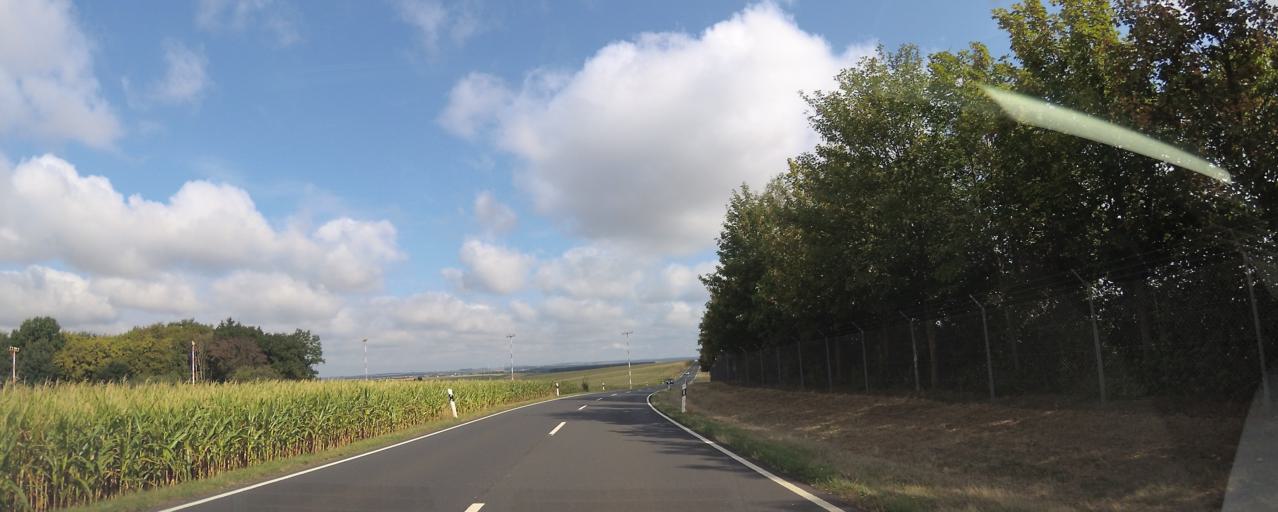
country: DE
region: Rheinland-Pfalz
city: Beilingen
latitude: 49.9612
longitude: 6.6770
